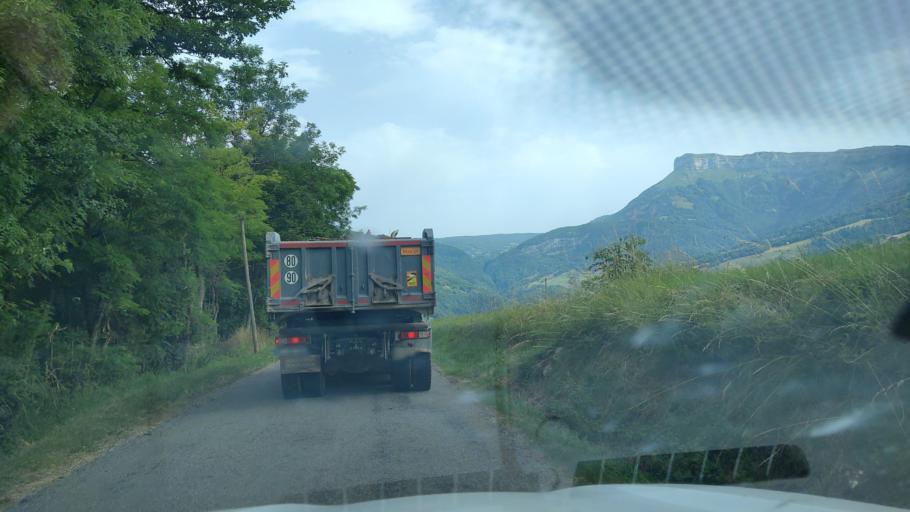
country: FR
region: Rhone-Alpes
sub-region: Departement de la Savoie
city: Barby
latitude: 45.5750
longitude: 6.0301
